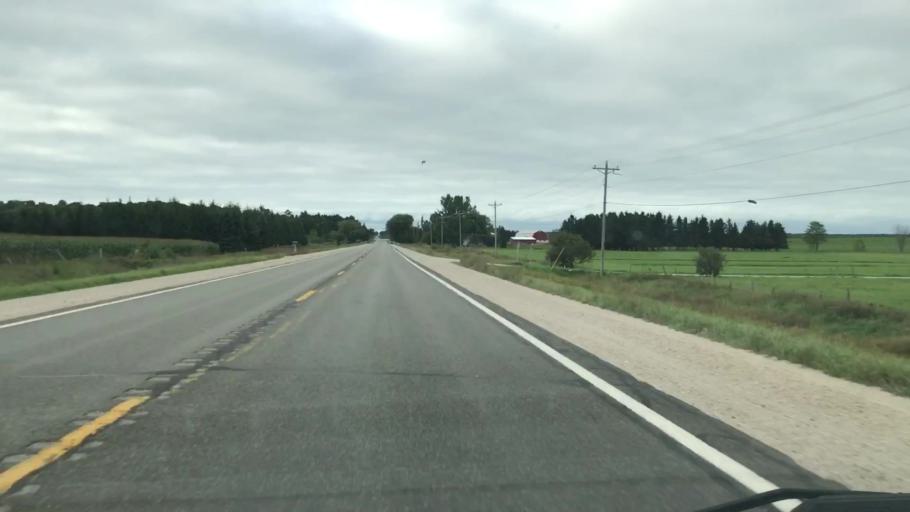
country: US
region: Michigan
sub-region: Luce County
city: Newberry
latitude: 46.1612
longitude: -85.5713
